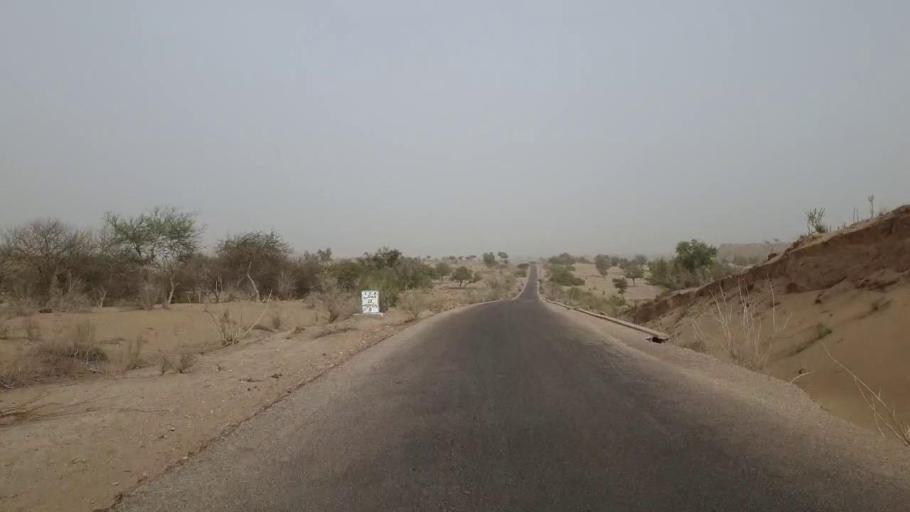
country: PK
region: Sindh
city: Islamkot
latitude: 24.5859
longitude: 70.2955
